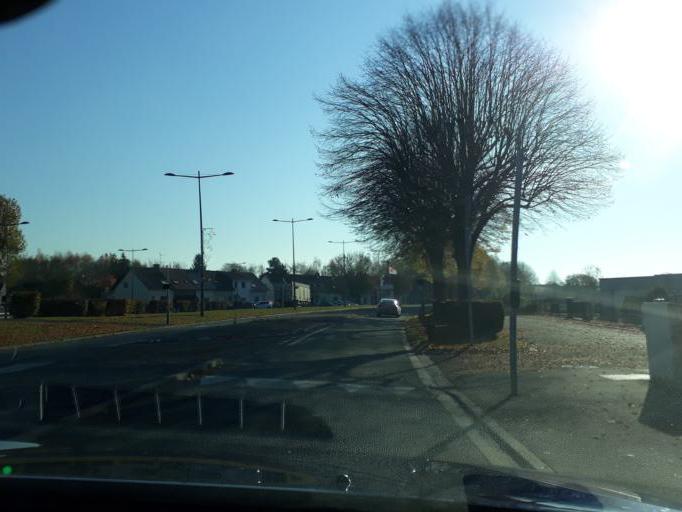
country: FR
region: Nord-Pas-de-Calais
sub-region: Departement du Nord
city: Masny
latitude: 50.3410
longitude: 3.2022
